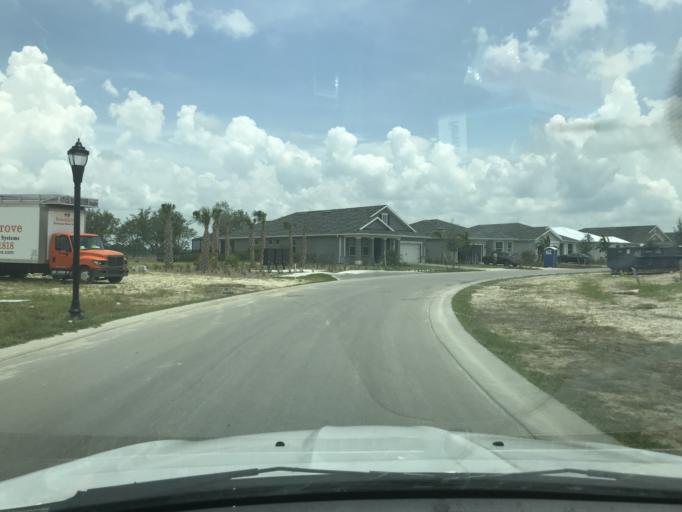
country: US
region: Florida
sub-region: Lee County
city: Olga
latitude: 26.7815
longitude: -81.7424
